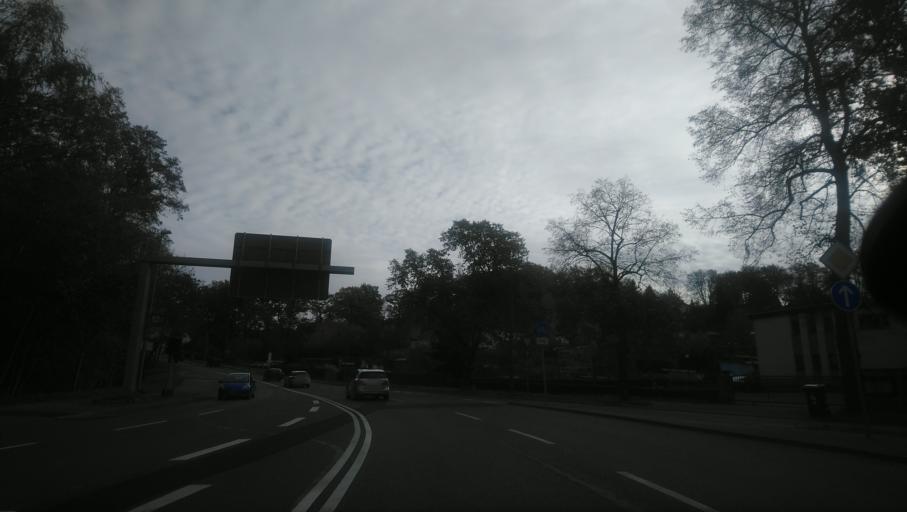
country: DE
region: Saxony
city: Wilkau-Hasslau
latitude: 50.7014
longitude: 12.5034
